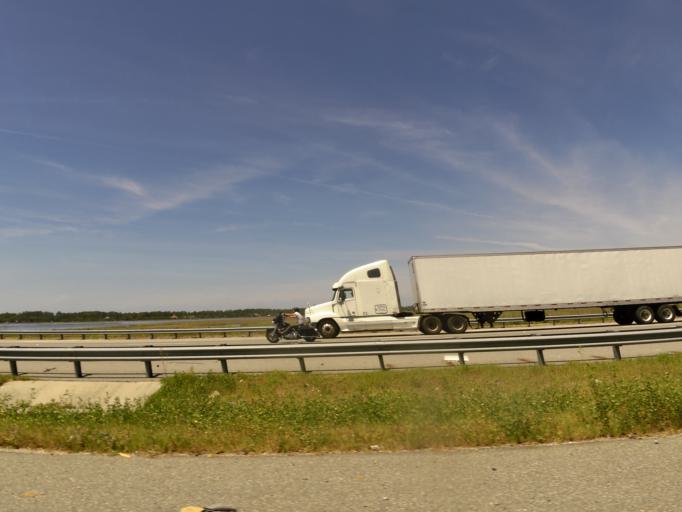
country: US
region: Georgia
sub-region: Glynn County
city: Dock Junction
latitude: 31.1974
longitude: -81.5381
